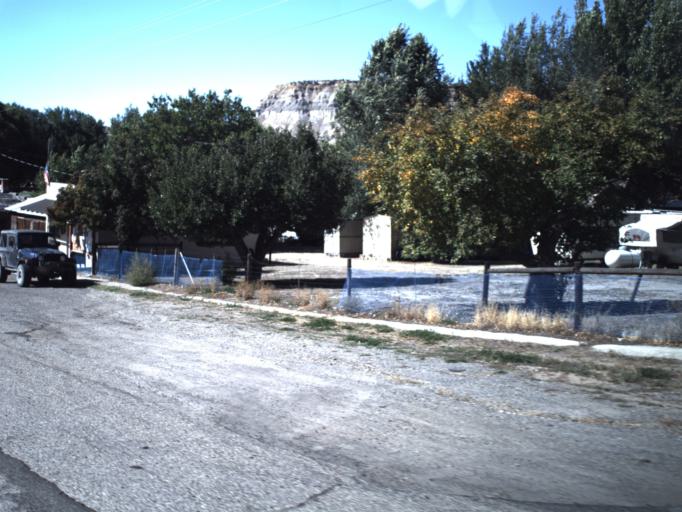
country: US
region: Utah
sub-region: Garfield County
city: Panguitch
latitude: 37.5625
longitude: -111.9936
